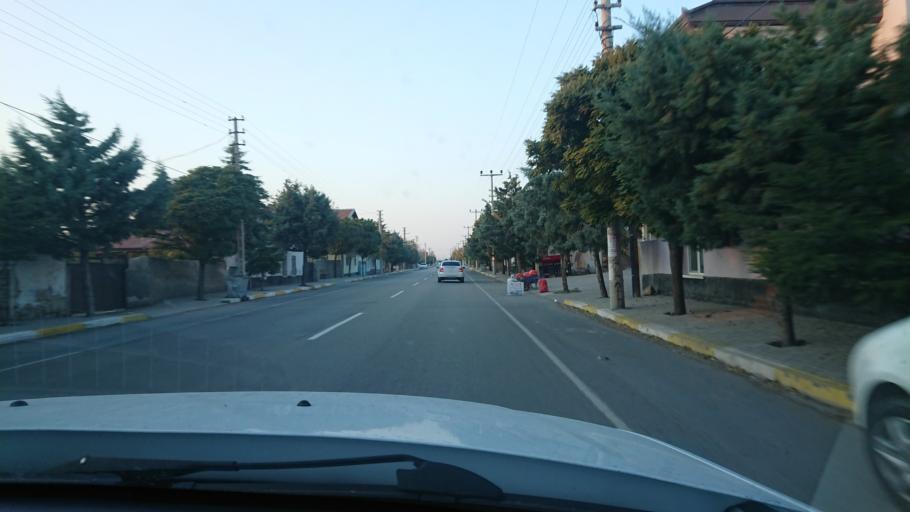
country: TR
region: Aksaray
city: Aksaray
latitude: 38.3055
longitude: 34.0684
